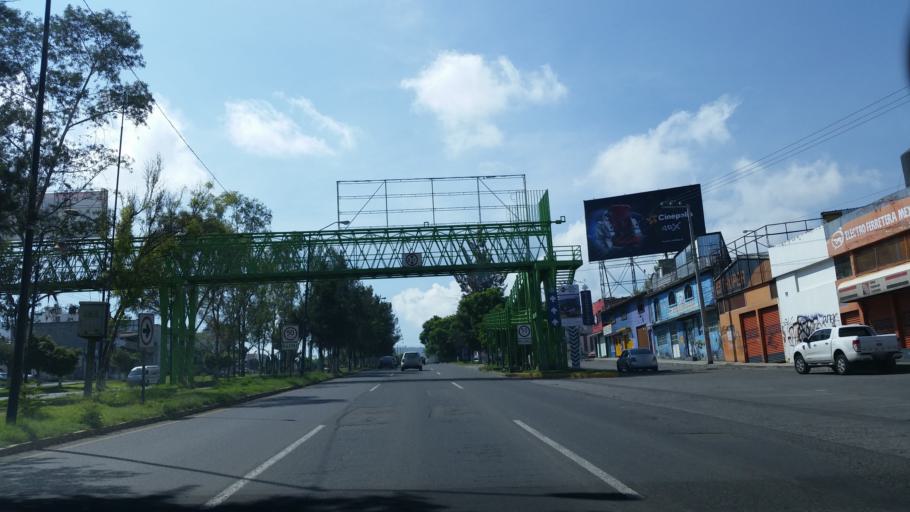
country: MX
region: Michoacan
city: Morelia
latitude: 19.7046
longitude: -101.1604
